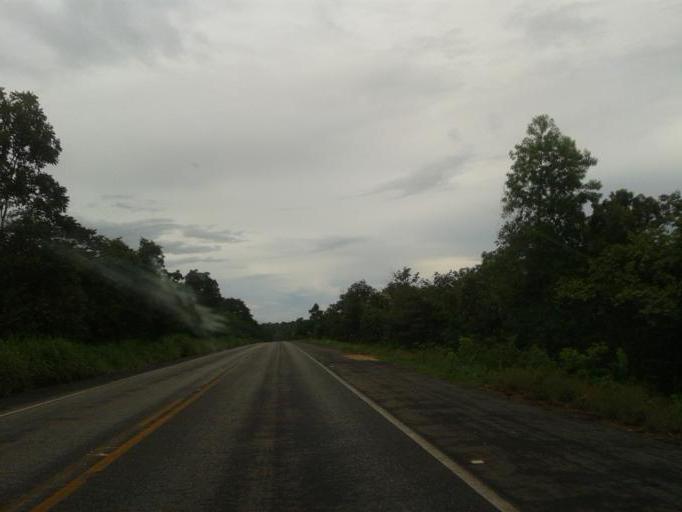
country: BR
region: Goias
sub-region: Mozarlandia
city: Mozarlandia
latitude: -14.8397
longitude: -50.5405
